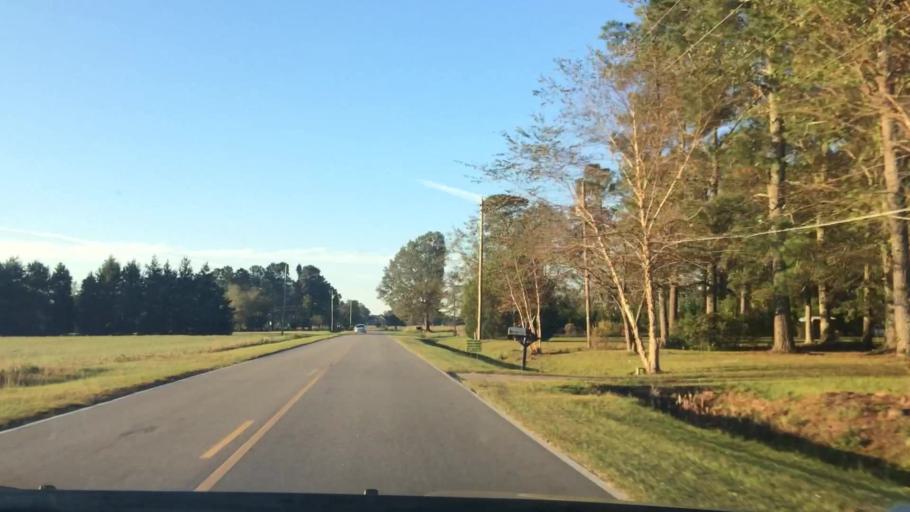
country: US
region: North Carolina
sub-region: Pitt County
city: Grifton
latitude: 35.3925
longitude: -77.4003
